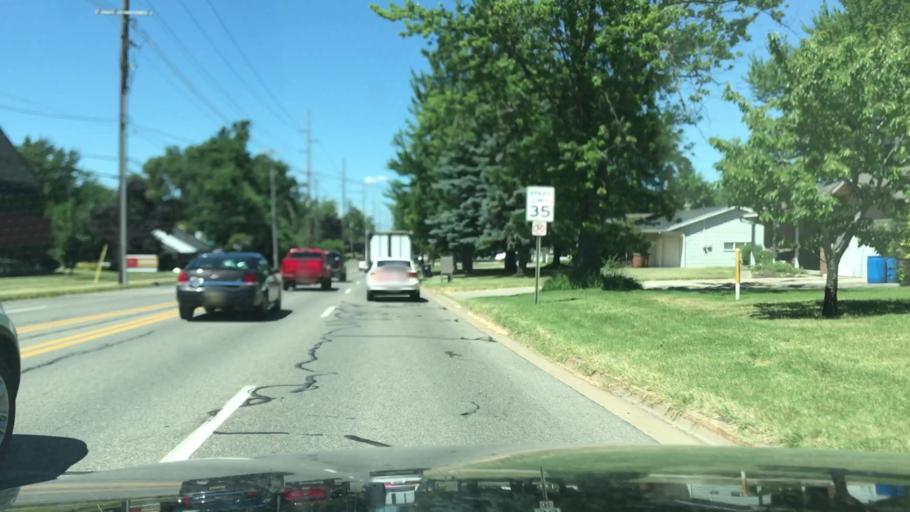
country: US
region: Michigan
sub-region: Ottawa County
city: Holland
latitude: 42.7843
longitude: -86.0775
